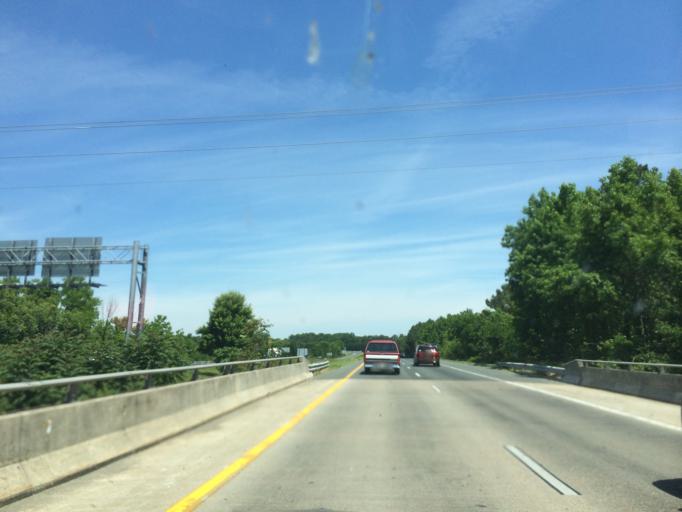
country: US
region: Maryland
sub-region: Wicomico County
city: Salisbury
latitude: 38.3803
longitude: -75.5399
